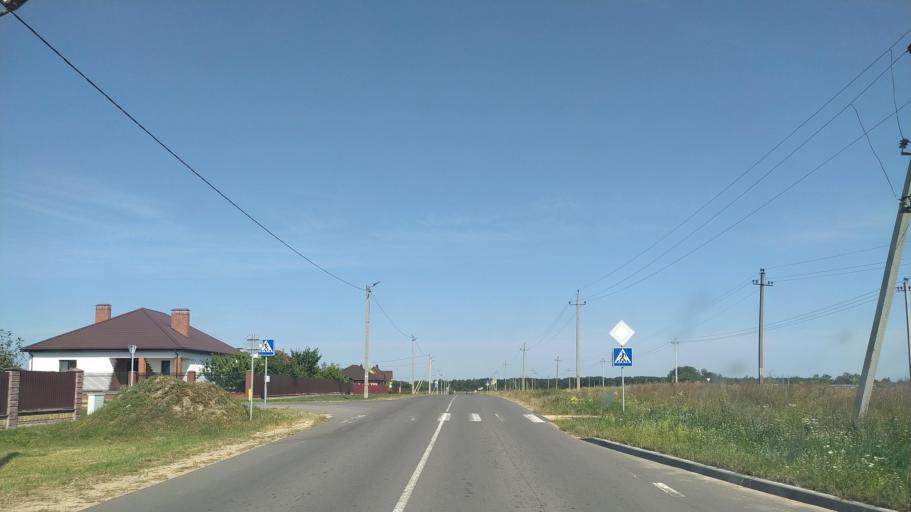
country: BY
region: Brest
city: Byaroza
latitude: 52.5194
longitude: 24.9833
